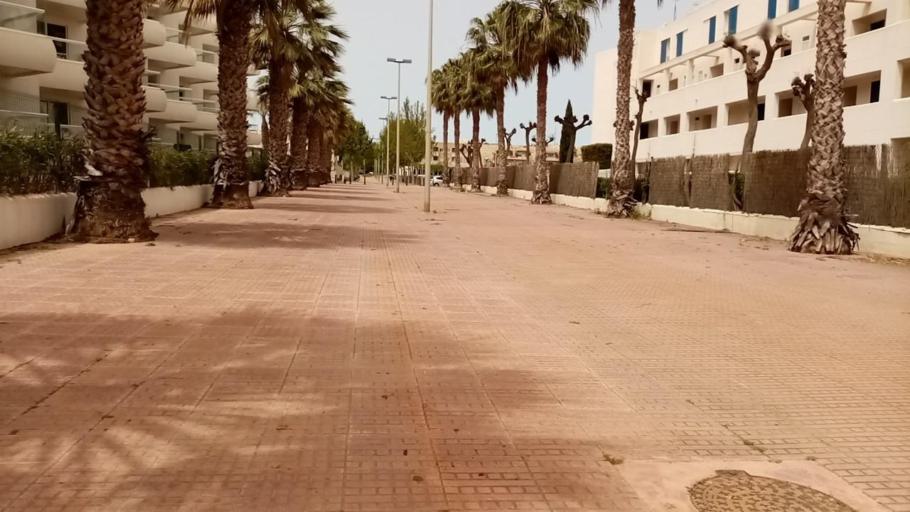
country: ES
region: Balearic Islands
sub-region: Illes Balears
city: Santa Eularia des Riu
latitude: 38.9881
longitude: 1.5457
